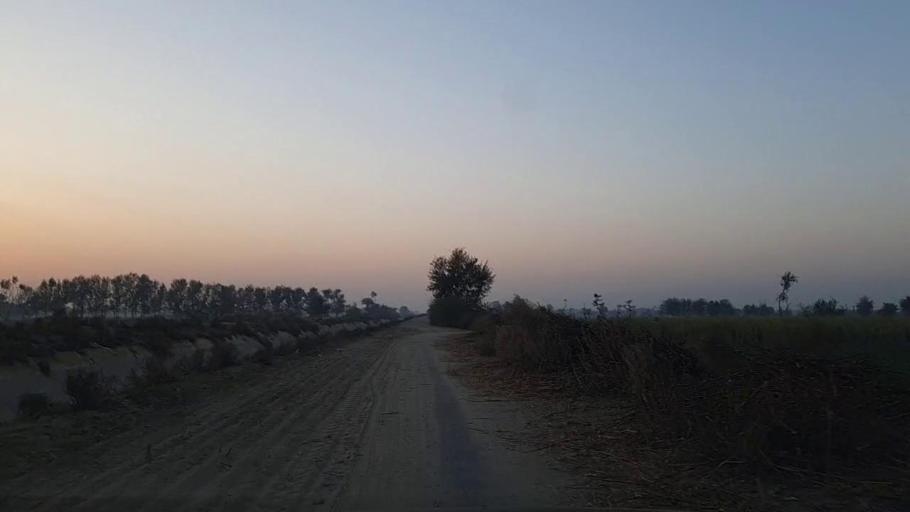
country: PK
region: Sindh
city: Daur
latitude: 26.4784
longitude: 68.4940
